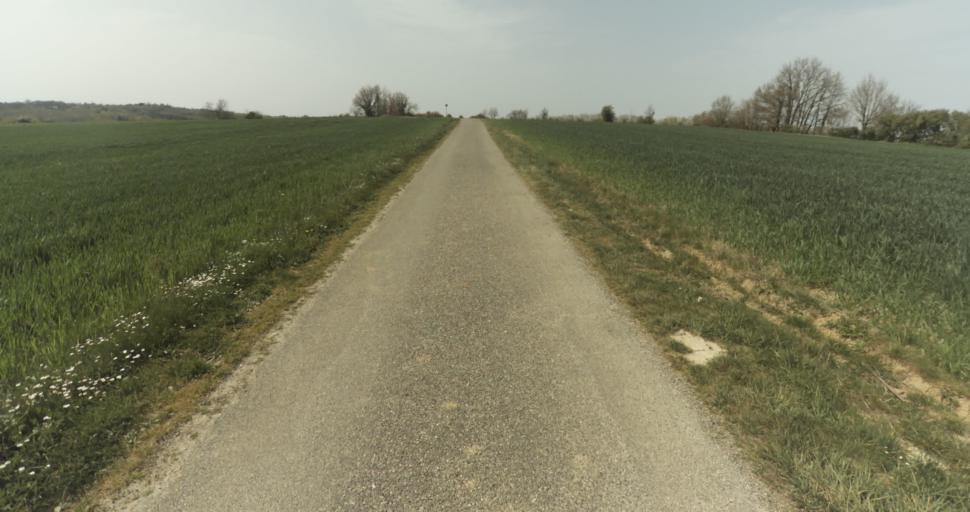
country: FR
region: Midi-Pyrenees
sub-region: Departement du Tarn-et-Garonne
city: Moissac
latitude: 44.1240
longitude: 1.1120
